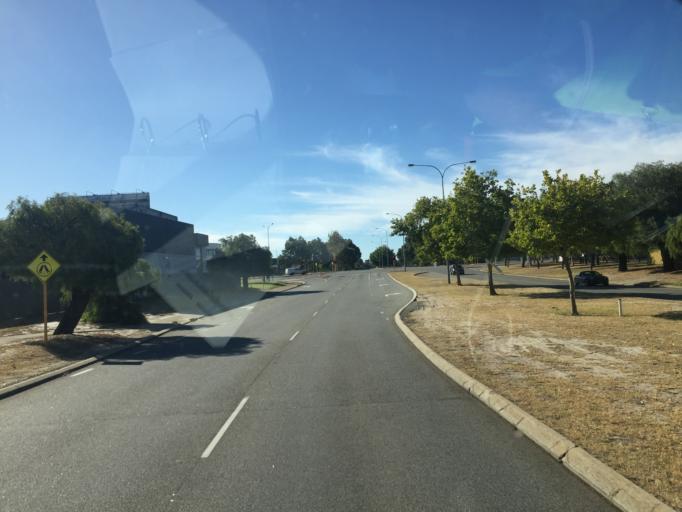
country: AU
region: Western Australia
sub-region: Canning
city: Queens Park
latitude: -31.9943
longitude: 115.9455
